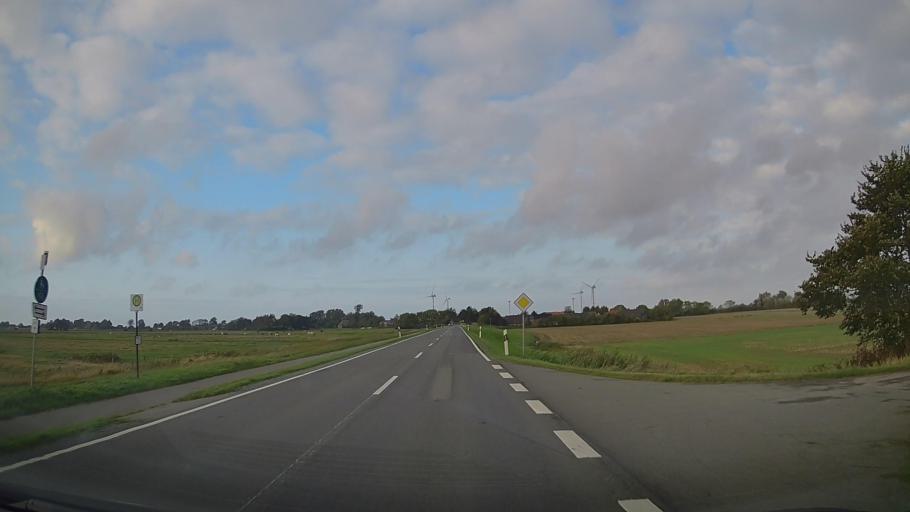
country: DE
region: Schleswig-Holstein
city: Simonsberg
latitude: 54.4285
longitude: 8.9743
